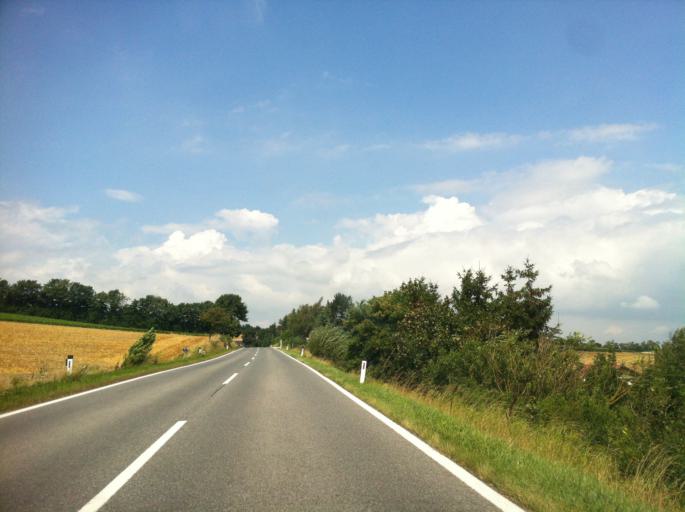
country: AT
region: Lower Austria
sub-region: Politischer Bezirk Tulln
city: Tulbing
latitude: 48.2676
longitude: 16.0745
